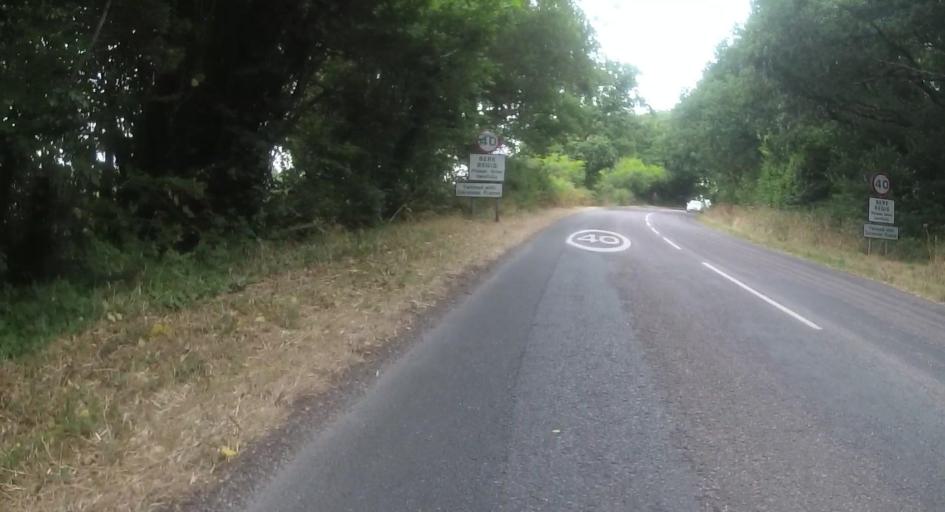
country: GB
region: England
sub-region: Dorset
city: Bovington Camp
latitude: 50.7412
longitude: -2.2201
